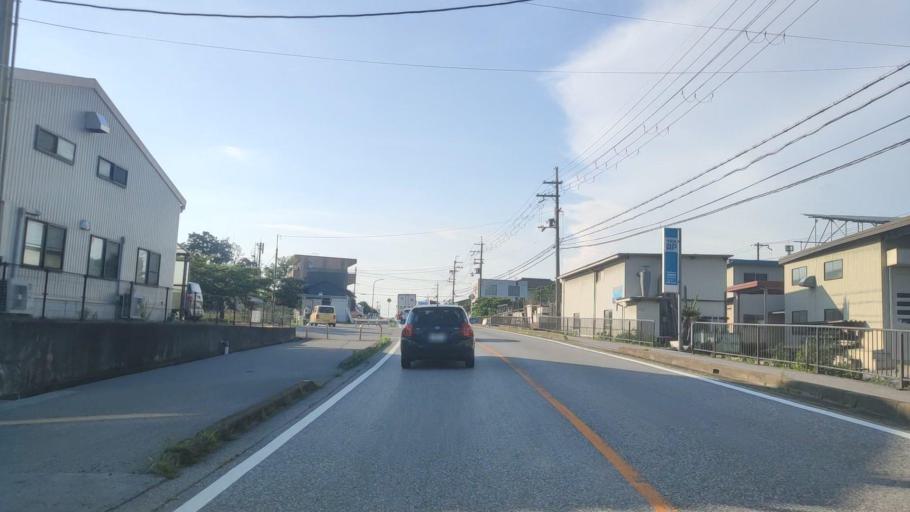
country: JP
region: Shiga Prefecture
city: Hikone
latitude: 35.2527
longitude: 136.2771
